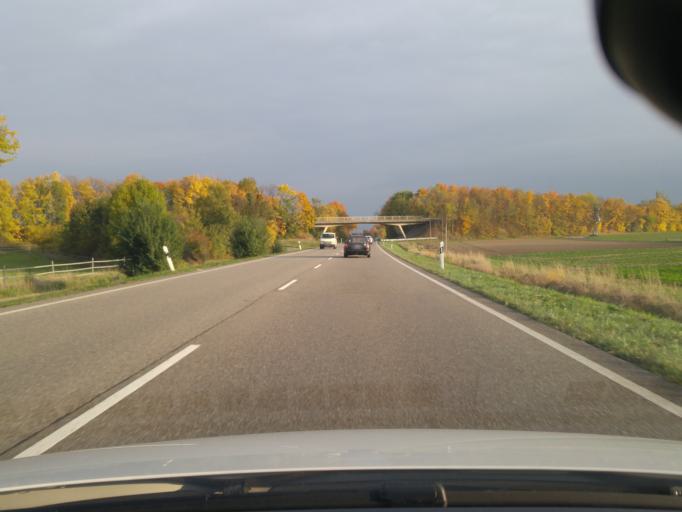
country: DE
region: Baden-Wuerttemberg
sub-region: Karlsruhe Region
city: Reilingen
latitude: 49.3007
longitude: 8.5785
